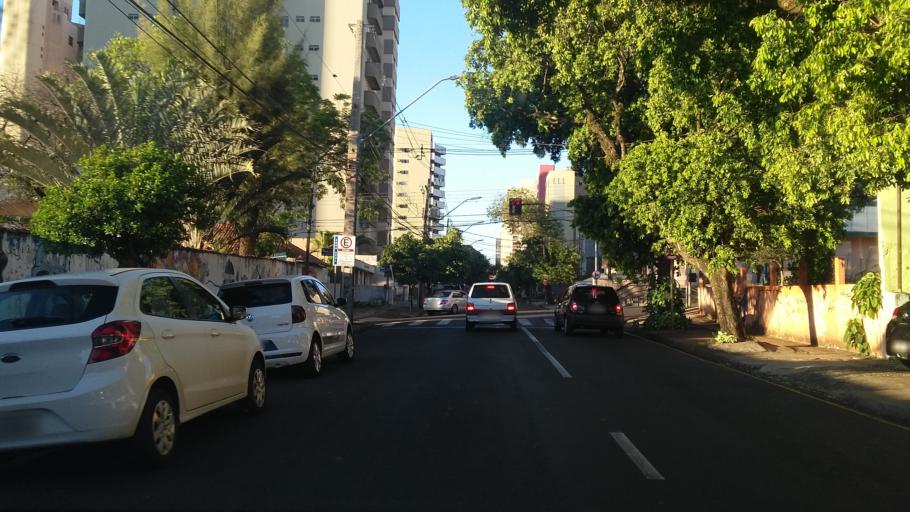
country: BR
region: Parana
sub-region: Londrina
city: Londrina
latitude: -23.3180
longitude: -51.1589
